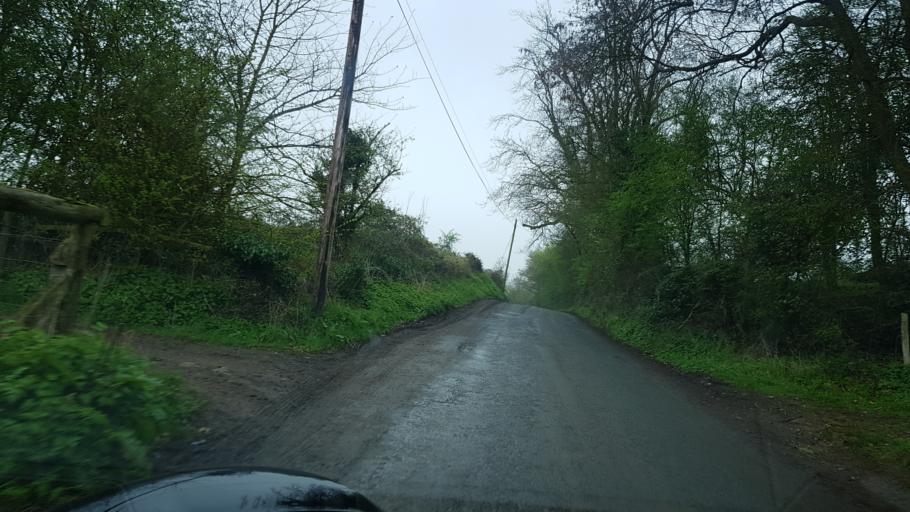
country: GB
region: England
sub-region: Herefordshire
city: Yatton
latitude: 52.0090
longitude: -2.5226
